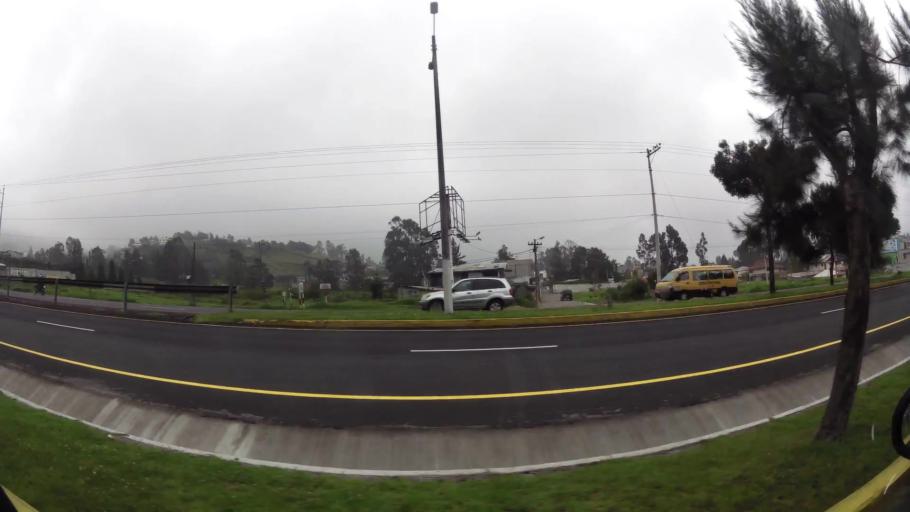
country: EC
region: Pichincha
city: Quito
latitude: -0.2780
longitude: -78.4834
